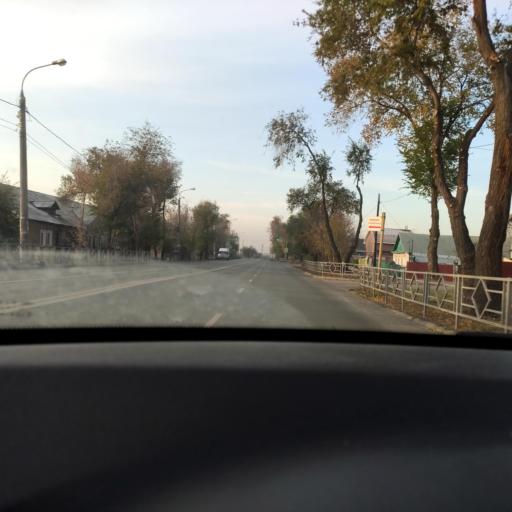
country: RU
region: Samara
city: Samara
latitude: 53.1836
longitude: 50.2002
